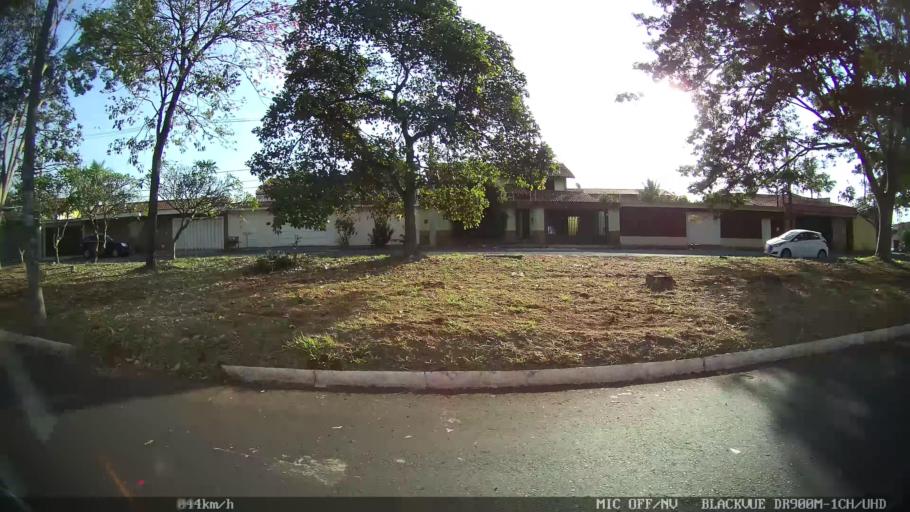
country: BR
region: Sao Paulo
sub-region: Ribeirao Preto
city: Ribeirao Preto
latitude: -21.1570
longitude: -47.8390
